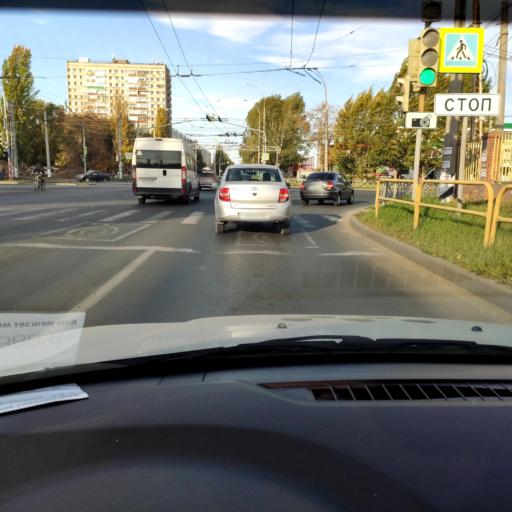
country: RU
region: Samara
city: Tol'yatti
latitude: 53.5362
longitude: 49.2998
